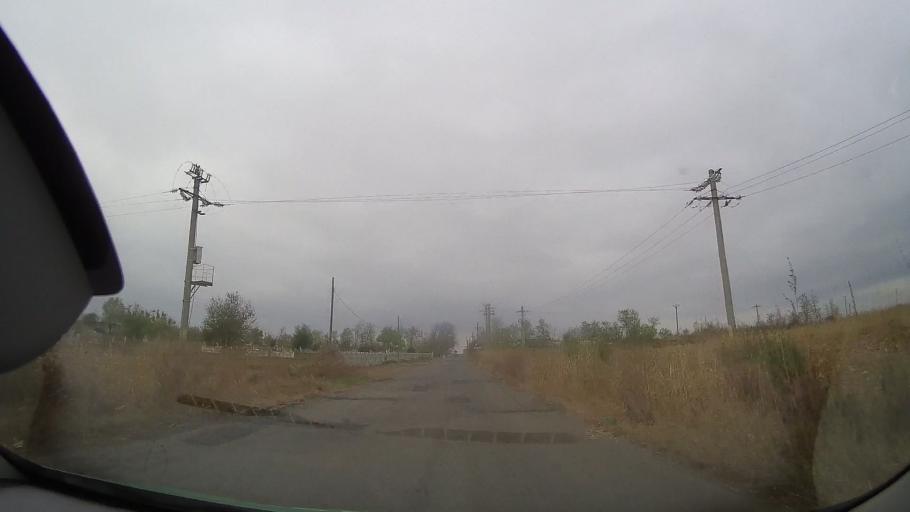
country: RO
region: Braila
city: Dudesti
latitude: 44.9401
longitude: 27.4250
